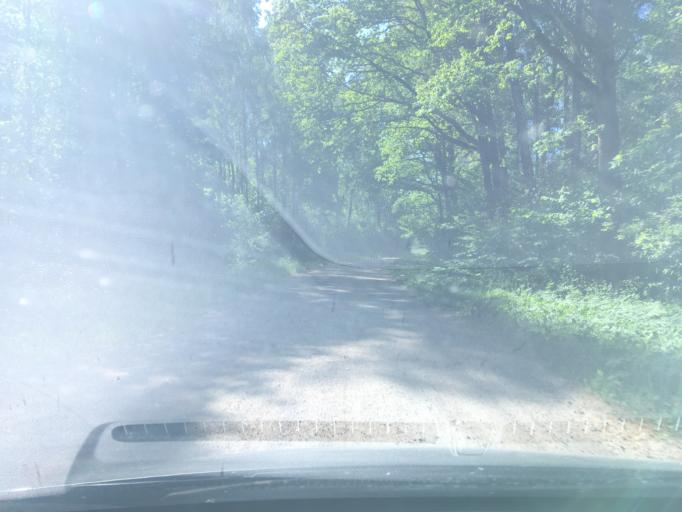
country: EE
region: Laeaene
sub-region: Lihula vald
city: Lihula
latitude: 58.6433
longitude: 23.7872
